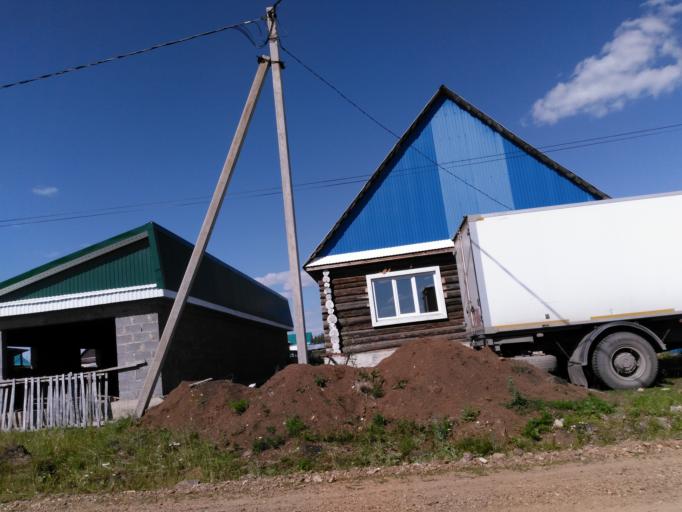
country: RU
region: Bashkortostan
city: Uchaly
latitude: 54.2922
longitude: 59.3656
